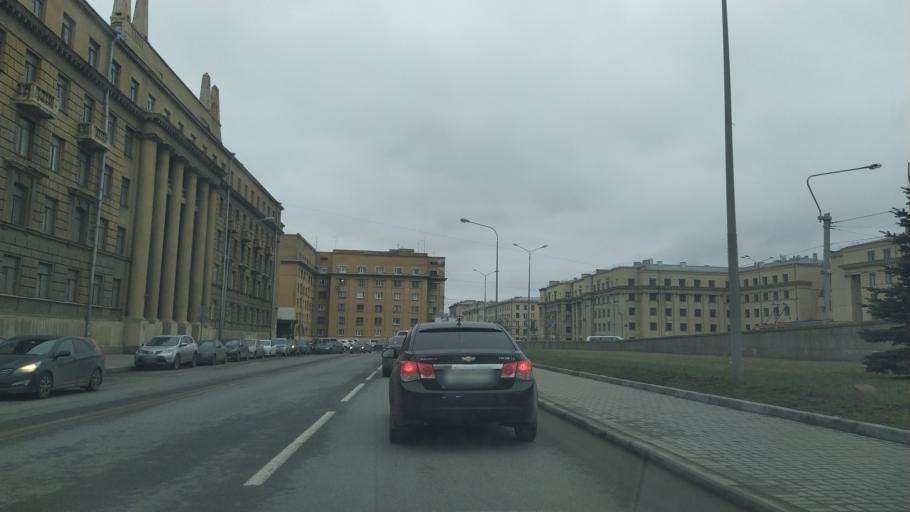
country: RU
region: St.-Petersburg
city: Centralniy
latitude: 59.9275
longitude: 30.4026
